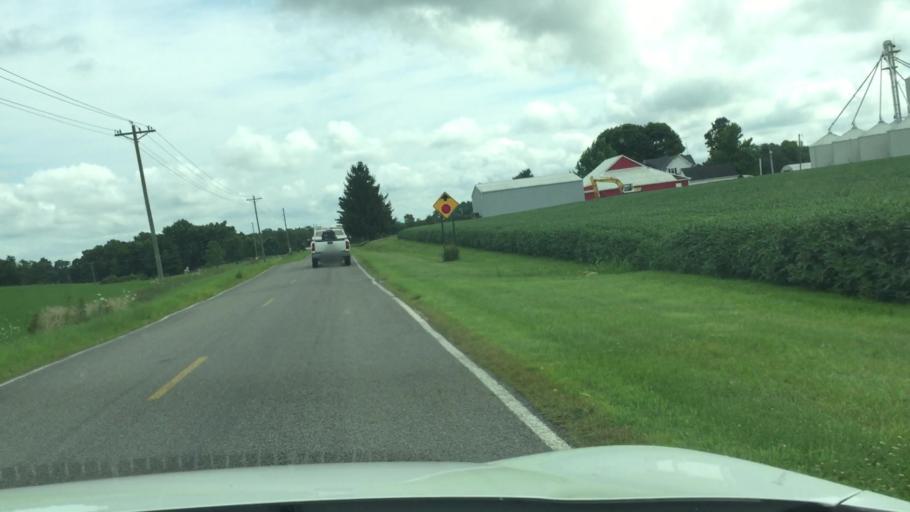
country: US
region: Ohio
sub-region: Champaign County
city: Mechanicsburg
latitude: 40.0345
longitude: -83.6565
